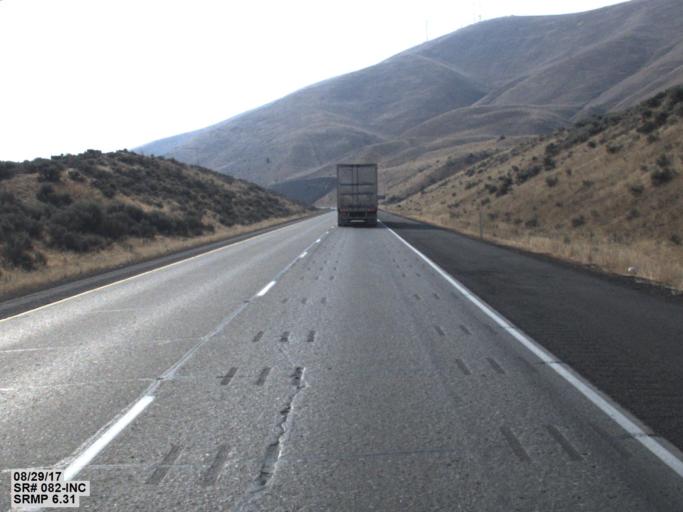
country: US
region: Washington
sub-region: Kittitas County
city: Kittitas
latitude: 46.8980
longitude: -120.4499
